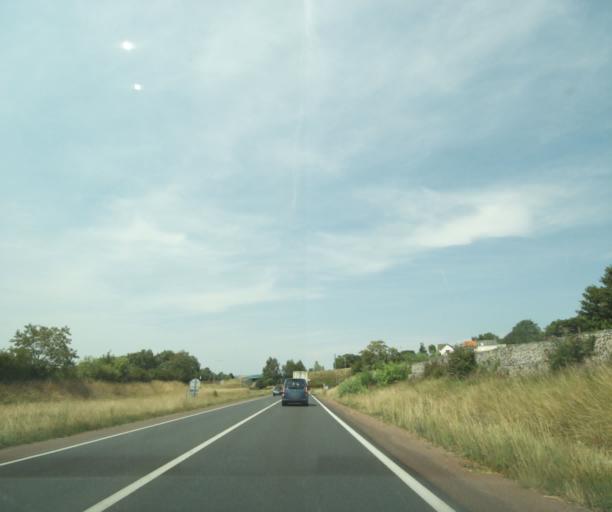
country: FR
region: Poitou-Charentes
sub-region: Departement de la Vienne
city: Chatellerault
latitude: 46.8172
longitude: 0.5667
